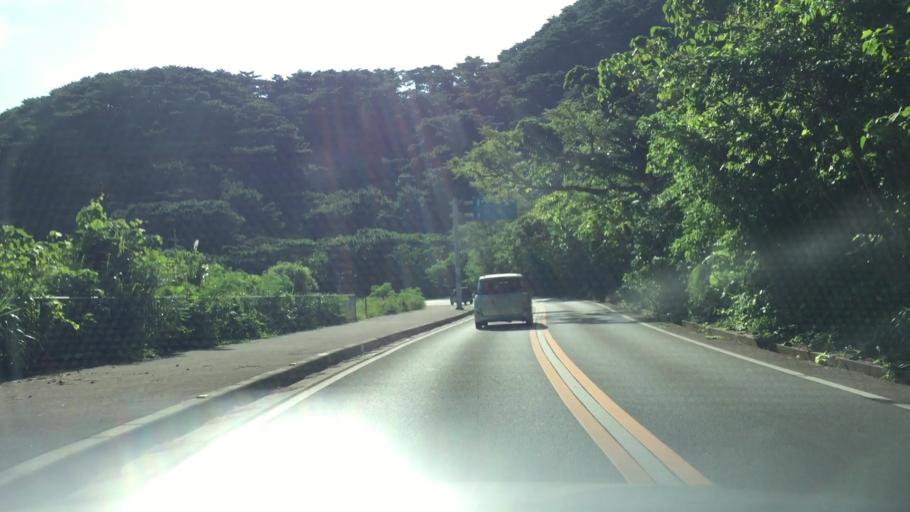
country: JP
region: Okinawa
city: Ishigaki
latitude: 24.4486
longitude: 124.1305
